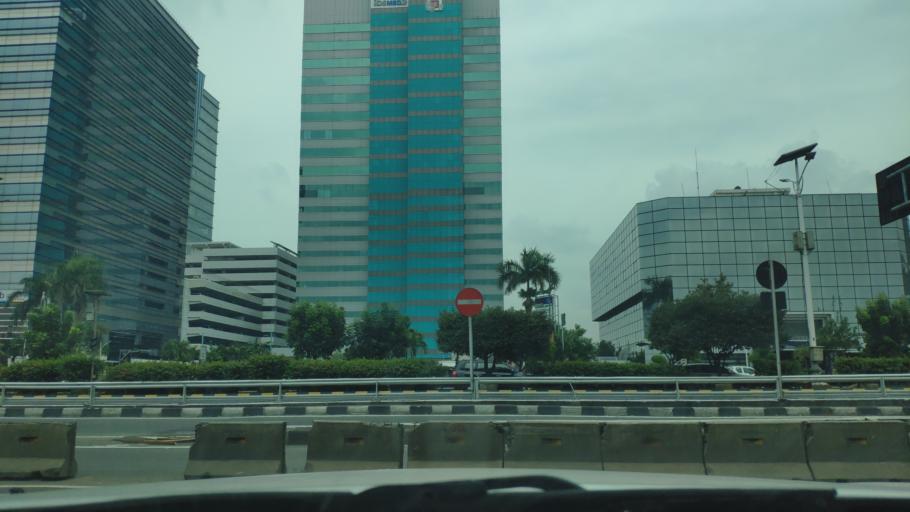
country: ID
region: Jakarta Raya
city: Jakarta
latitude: -6.1911
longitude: 106.7969
